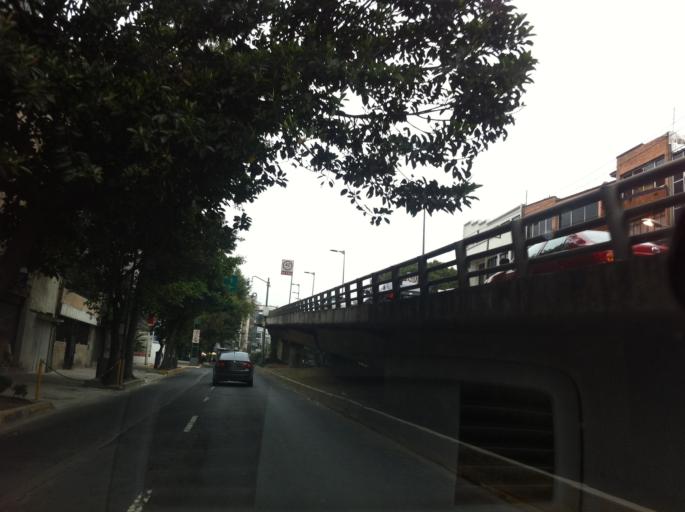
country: MX
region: Mexico City
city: Colonia del Valle
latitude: 19.3854
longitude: -99.1793
